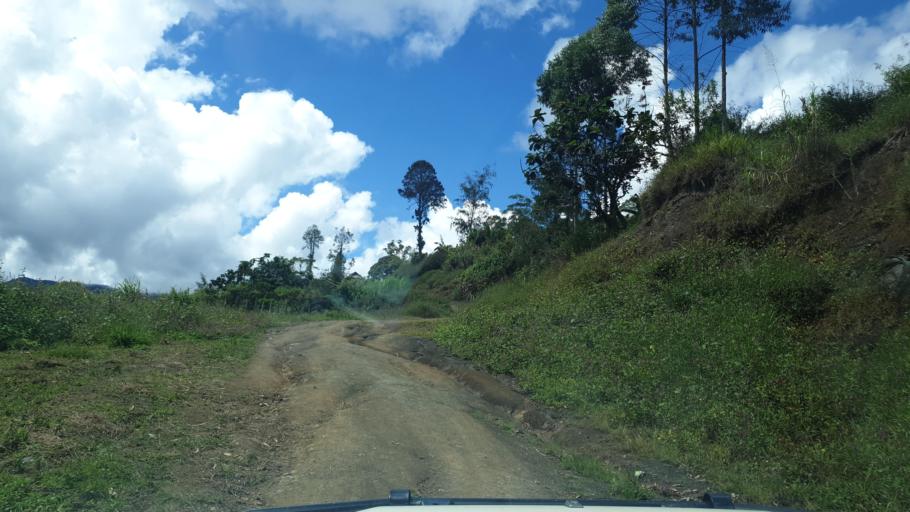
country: PG
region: Eastern Highlands
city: Goroka
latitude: -6.2769
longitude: 145.1864
